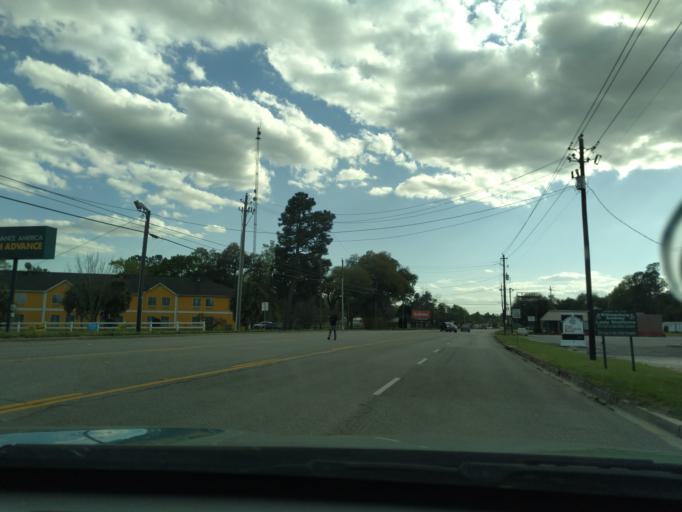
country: US
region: South Carolina
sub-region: Williamsburg County
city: Kingstree
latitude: 33.6840
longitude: -79.8234
